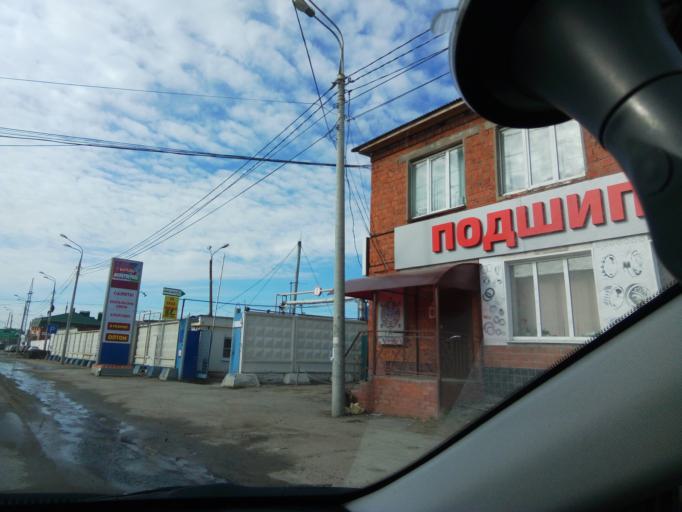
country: RU
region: Chuvashia
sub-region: Cheboksarskiy Rayon
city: Cheboksary
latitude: 56.1061
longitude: 47.2486
